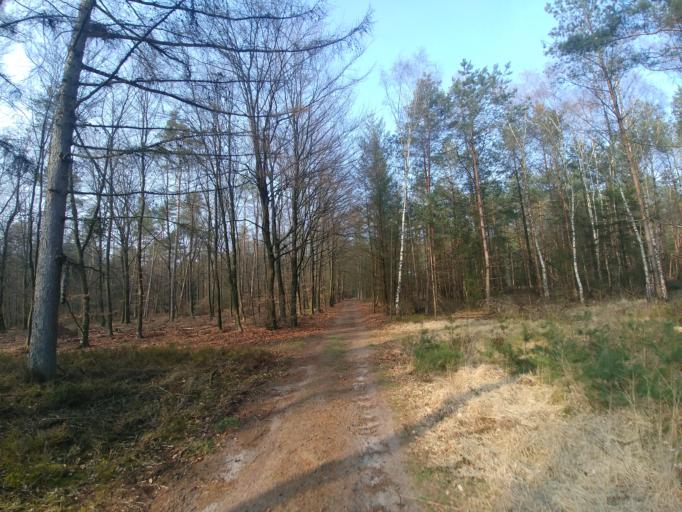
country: NL
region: Gelderland
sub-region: Gemeente Epe
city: Emst
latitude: 52.3472
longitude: 5.8810
